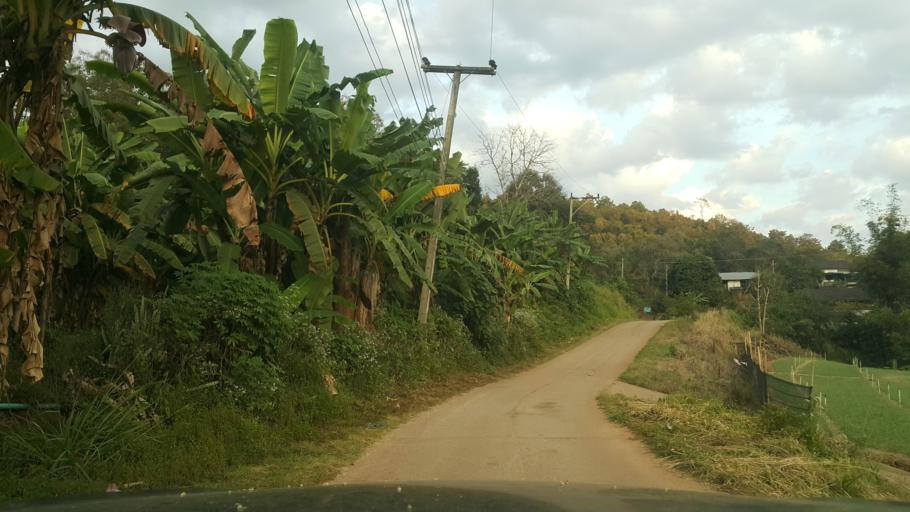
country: TH
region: Chiang Mai
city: Samoeng
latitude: 18.9743
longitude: 98.6817
